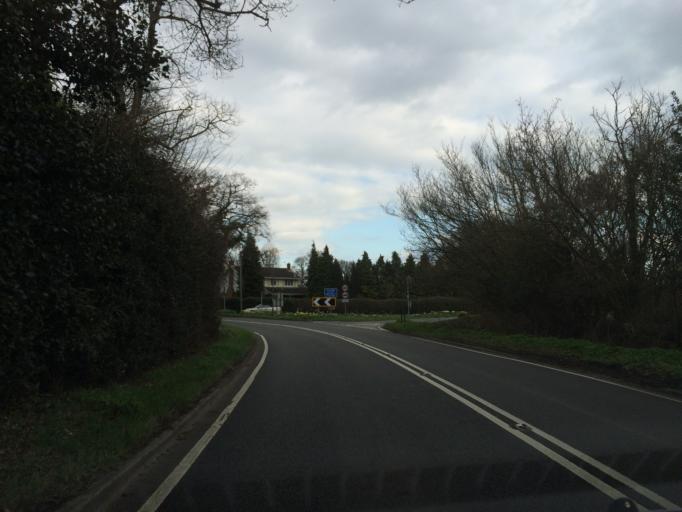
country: GB
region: England
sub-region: Surrey
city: Woking
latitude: 51.3489
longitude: -0.5709
